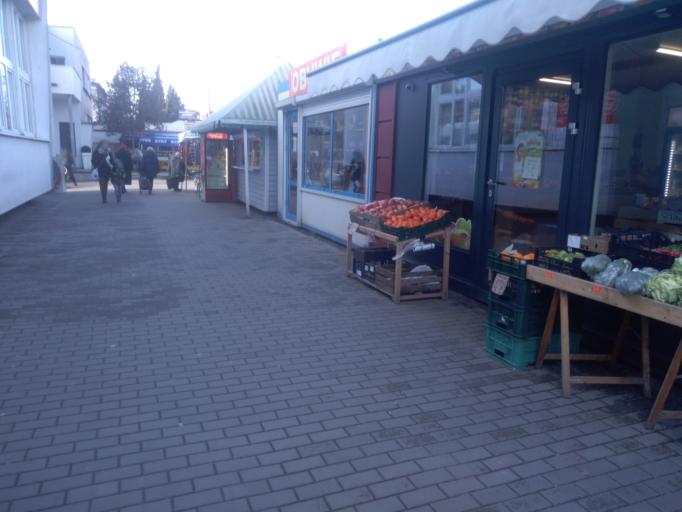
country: PL
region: Greater Poland Voivodeship
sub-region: Poznan
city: Poznan
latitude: 52.4173
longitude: 16.8821
